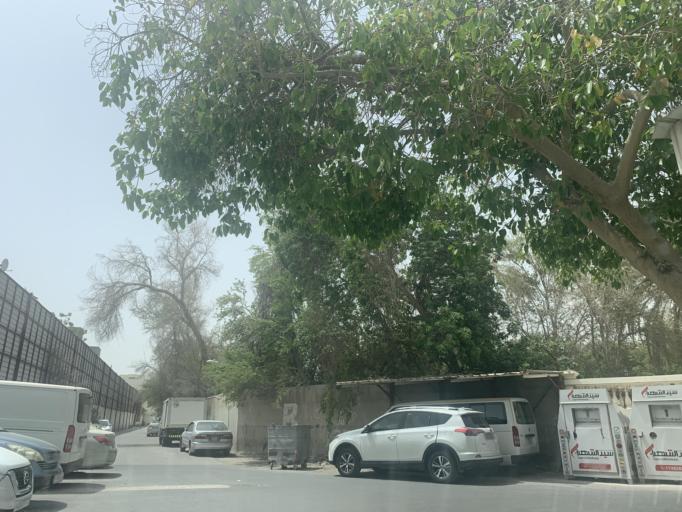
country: BH
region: Manama
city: Jidd Hafs
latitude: 26.2107
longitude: 50.5458
